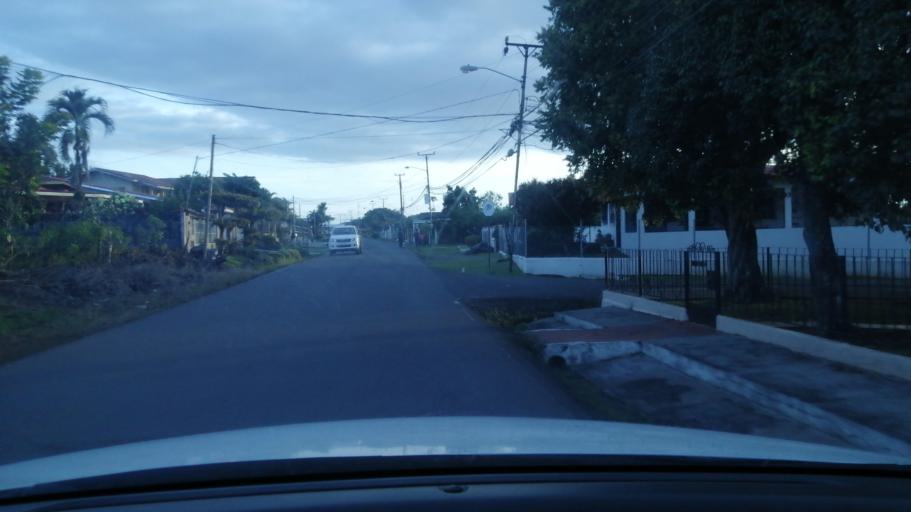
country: PA
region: Chiriqui
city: David
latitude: 8.4109
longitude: -82.4328
